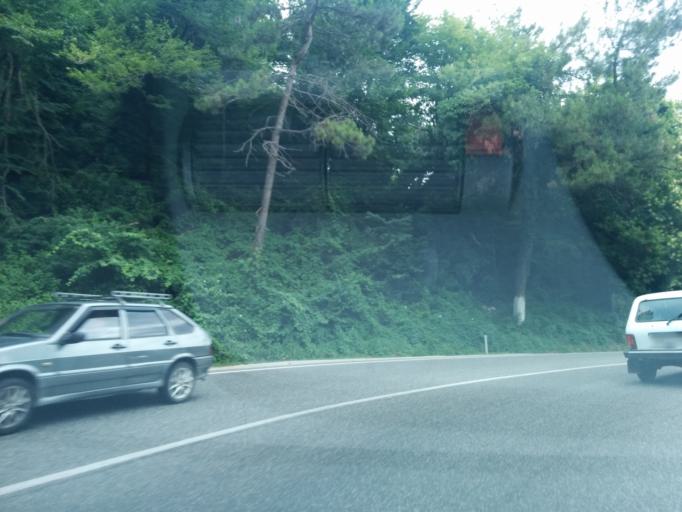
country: RU
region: Krasnodarskiy
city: Agoy
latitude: 44.1190
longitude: 39.0489
